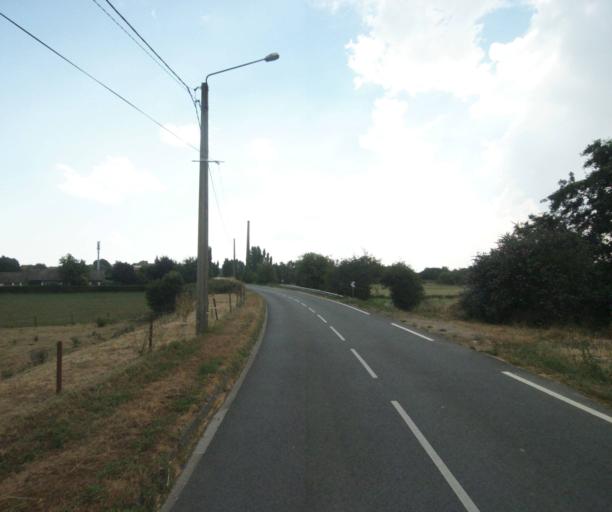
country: FR
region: Nord-Pas-de-Calais
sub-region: Departement du Nord
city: Deulemont
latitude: 50.7396
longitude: 2.9428
